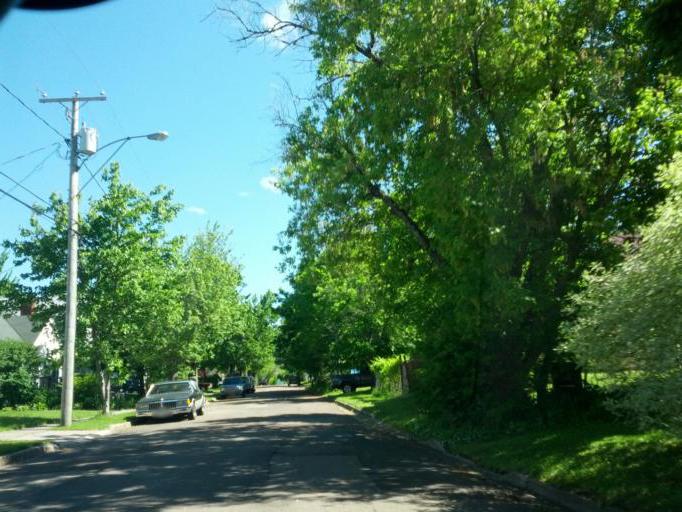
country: CA
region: New Brunswick
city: Moncton
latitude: 46.1000
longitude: -64.7926
